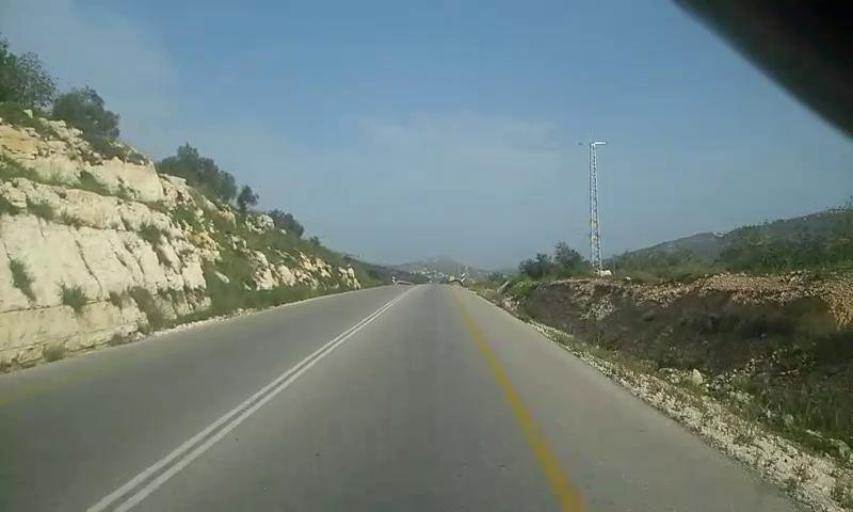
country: PS
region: West Bank
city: Till
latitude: 32.1898
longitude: 35.2083
